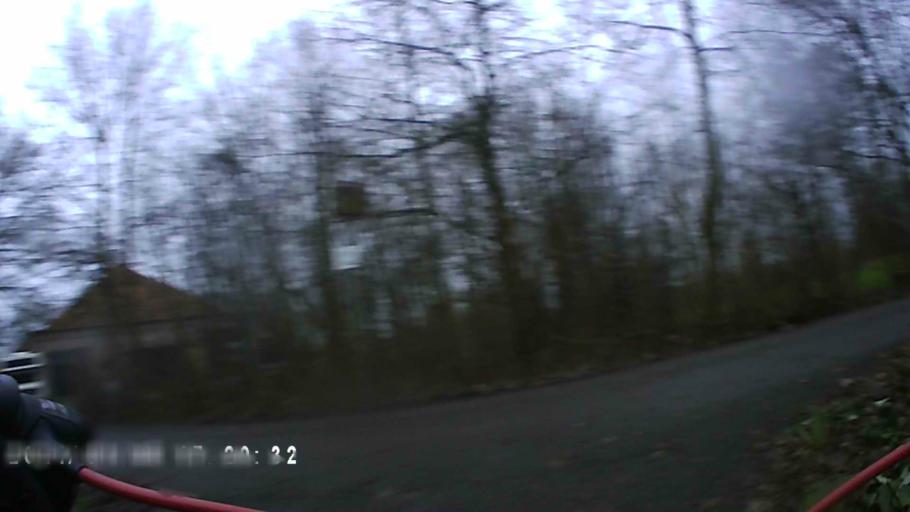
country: NL
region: Groningen
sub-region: Gemeente Delfzijl
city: Delfzijl
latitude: 53.2354
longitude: 6.9645
